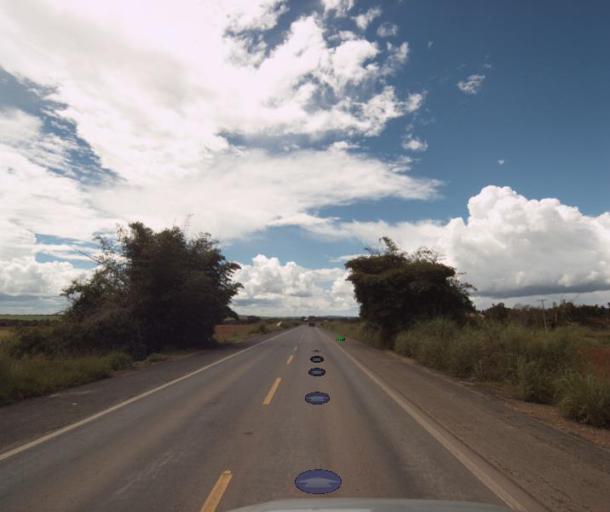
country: BR
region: Goias
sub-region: Uruacu
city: Uruacu
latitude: -14.1587
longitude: -49.1221
